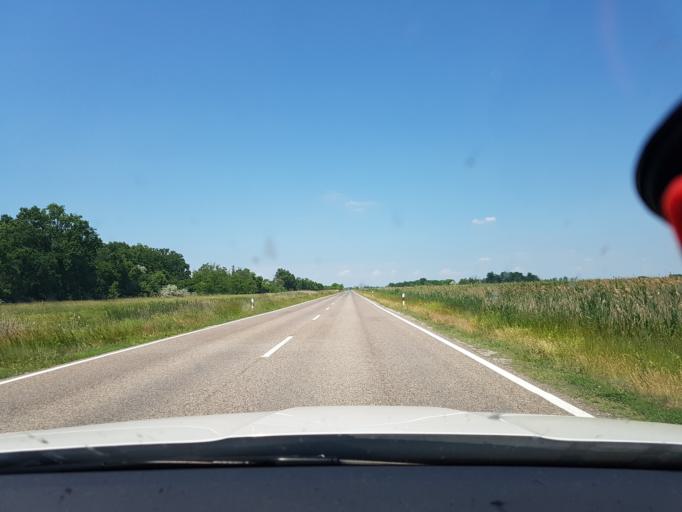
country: HU
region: Hajdu-Bihar
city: Egyek
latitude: 47.5624
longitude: 20.8633
